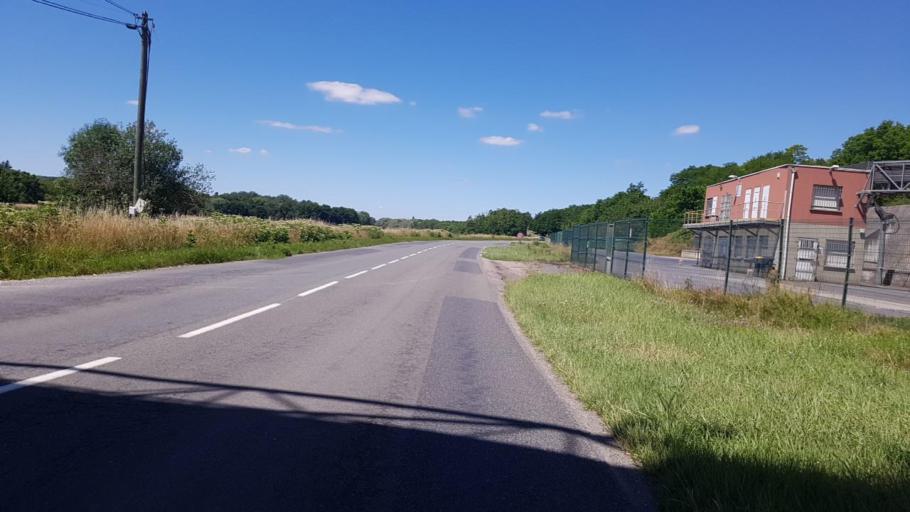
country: FR
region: Ile-de-France
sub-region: Departement de Seine-et-Marne
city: Sammeron
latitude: 48.9523
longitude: 3.1013
